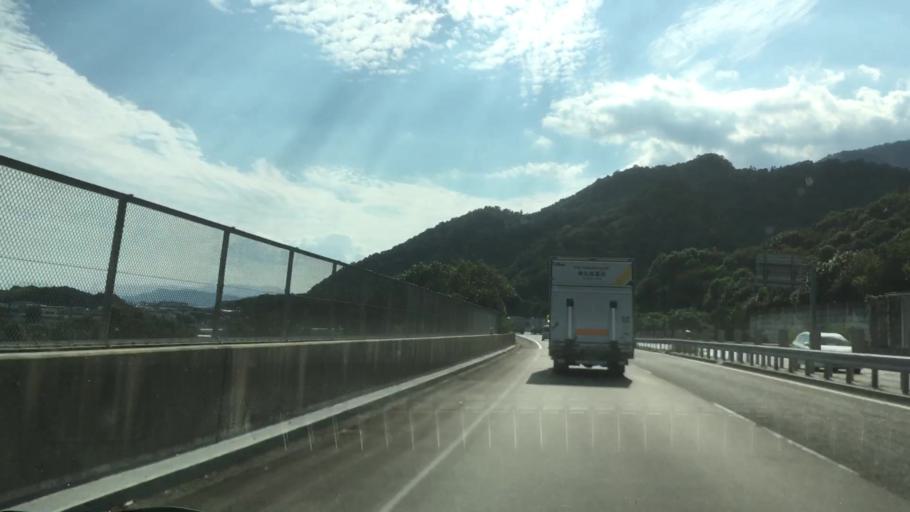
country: JP
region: Hiroshima
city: Ono-hara
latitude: 34.2988
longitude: 132.2720
